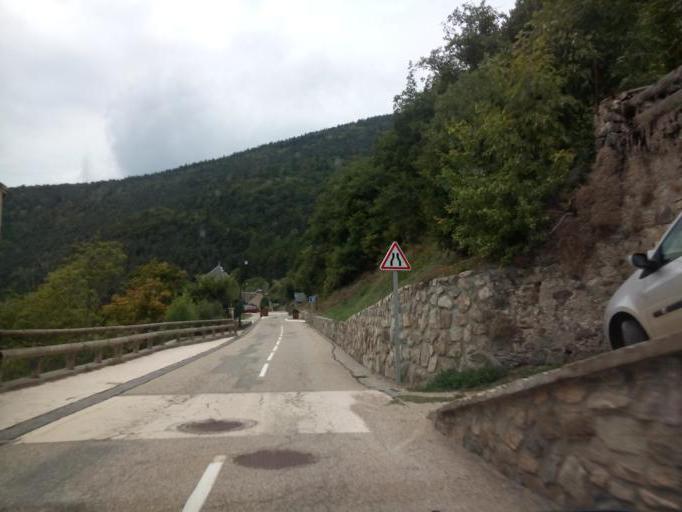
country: FR
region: Rhone-Alpes
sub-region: Departement de l'Isere
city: La Mure
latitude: 44.9408
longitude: 5.8547
